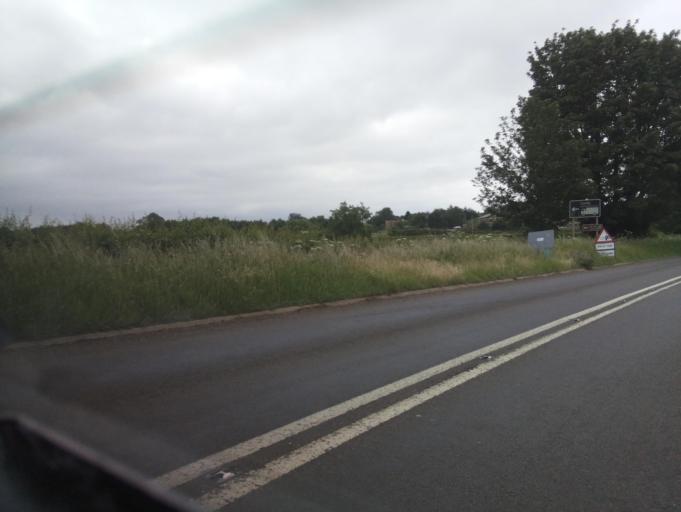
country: GB
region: England
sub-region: District of Rutland
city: Uppingham
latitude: 52.5980
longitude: -0.7235
